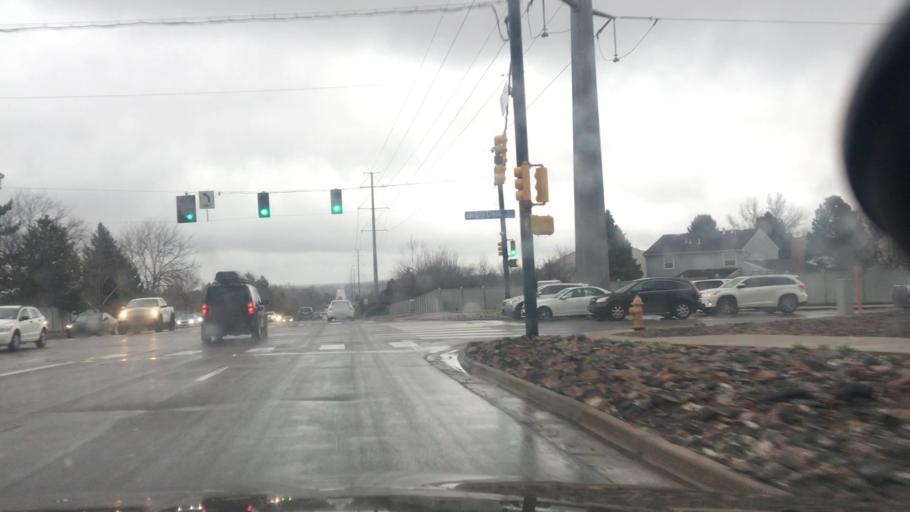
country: US
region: Colorado
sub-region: Arapahoe County
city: Castlewood
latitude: 39.5803
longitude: -104.9229
